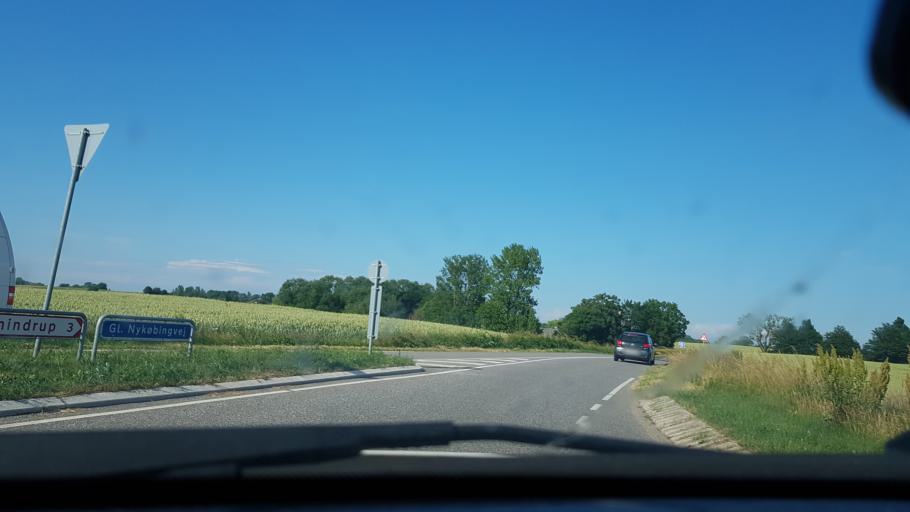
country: DK
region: Zealand
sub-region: Odsherred Kommune
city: Hojby
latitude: 55.8568
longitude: 11.5913
